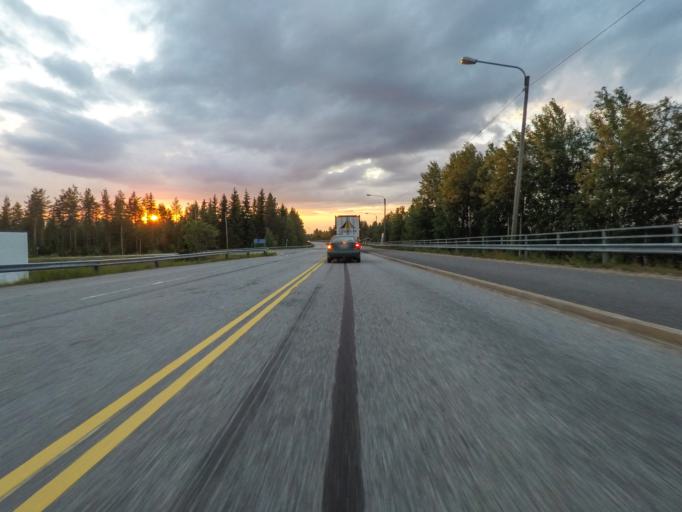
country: FI
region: Central Finland
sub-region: Jyvaeskylae
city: Hankasalmi
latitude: 62.3122
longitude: 26.4945
